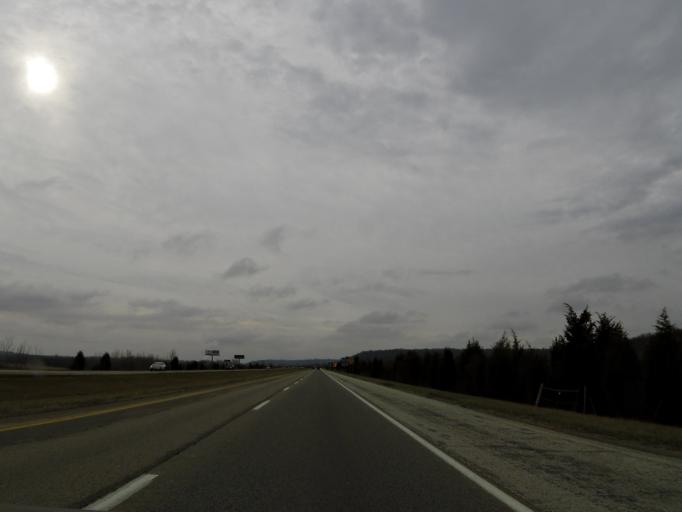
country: US
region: Indiana
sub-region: Dearborn County
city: Hidden Valley
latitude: 39.1430
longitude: -84.8237
